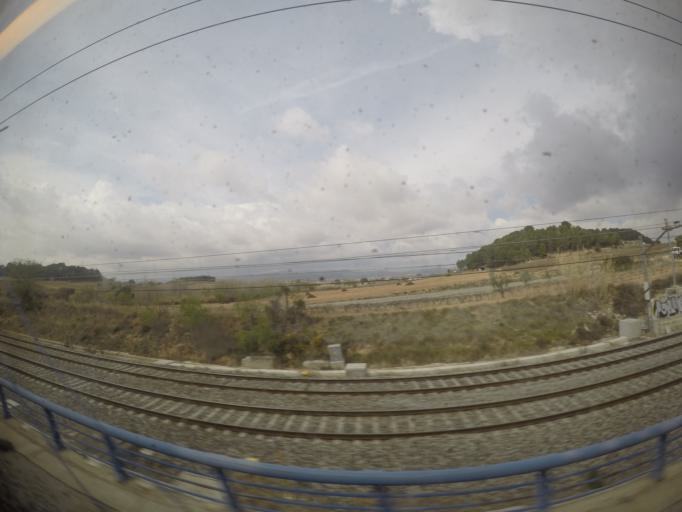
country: ES
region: Catalonia
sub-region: Provincia de Barcelona
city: Castellet
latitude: 41.2748
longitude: 1.6014
